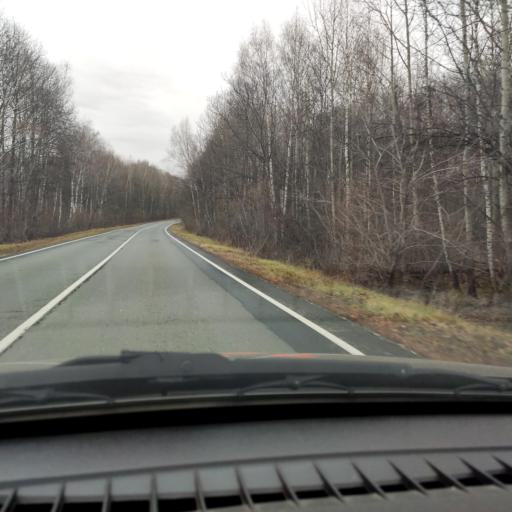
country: RU
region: Samara
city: Zhigulevsk
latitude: 53.3392
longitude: 49.5131
